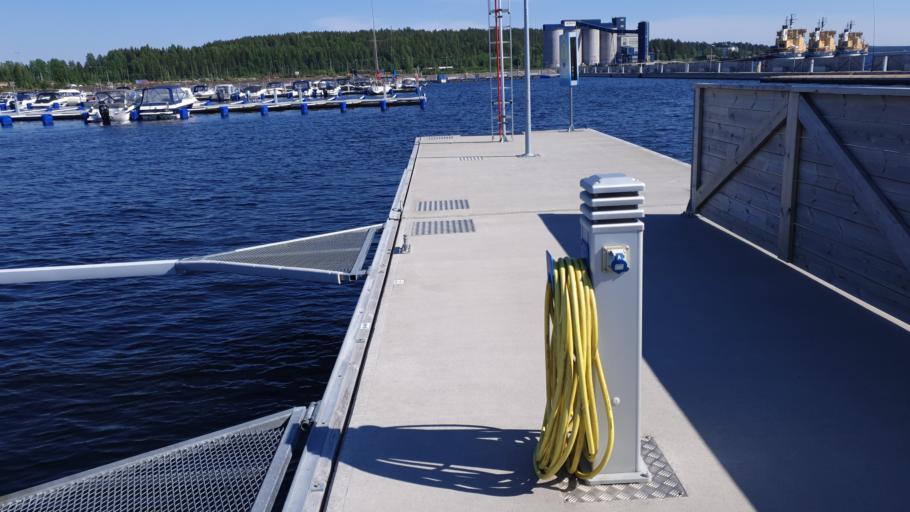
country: SE
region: Norrbotten
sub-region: Lulea Kommun
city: Lulea
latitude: 65.5783
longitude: 22.1625
